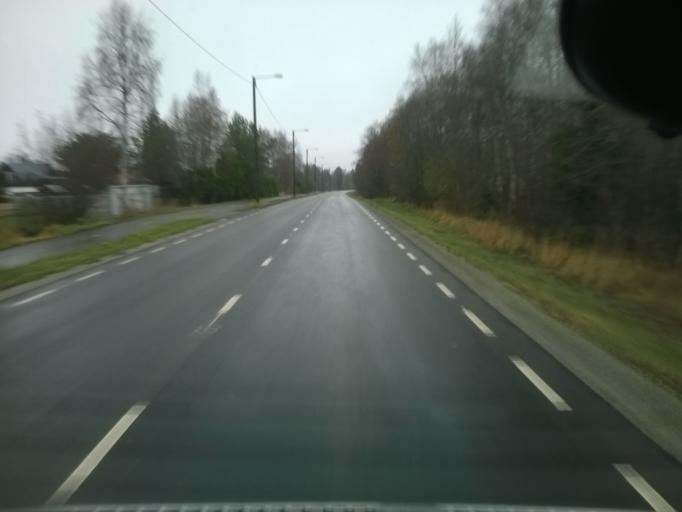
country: EE
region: Harju
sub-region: Saku vald
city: Saku
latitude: 59.2071
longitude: 24.6648
